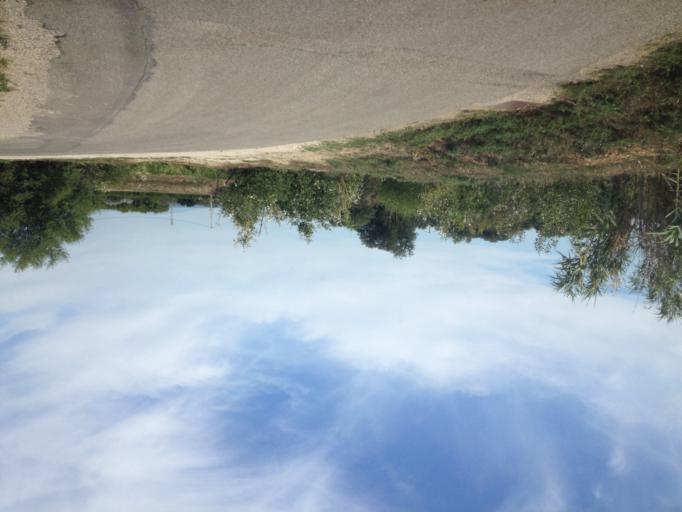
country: FR
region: Provence-Alpes-Cote d'Azur
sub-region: Departement du Vaucluse
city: Bedarrides
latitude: 44.0549
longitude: 4.8914
